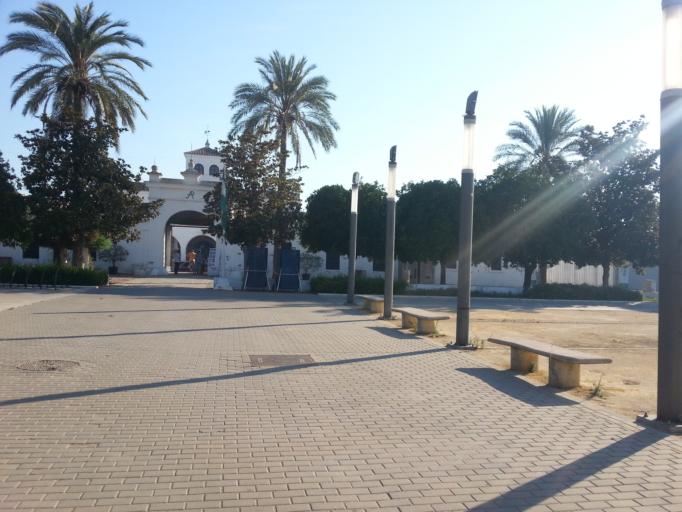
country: ES
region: Andalusia
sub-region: Provincia de Sevilla
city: Camas
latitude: 37.4209
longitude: -5.9960
